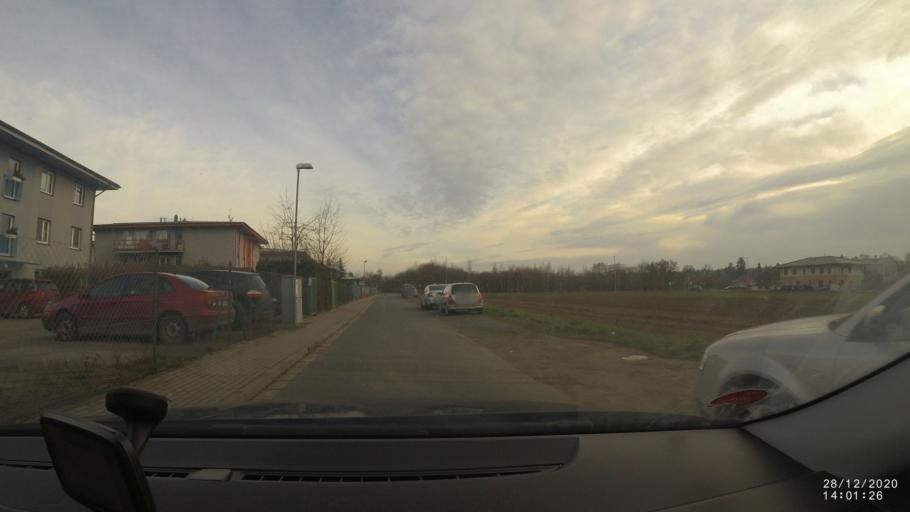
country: CZ
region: Central Bohemia
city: Sestajovice
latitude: 50.1025
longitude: 14.6739
